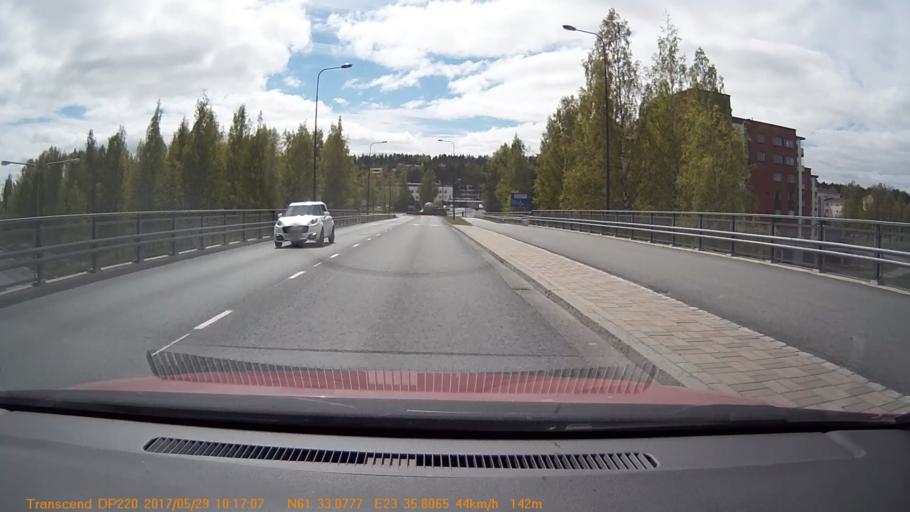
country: FI
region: Pirkanmaa
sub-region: Tampere
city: Yloejaervi
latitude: 61.5513
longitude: 23.5972
